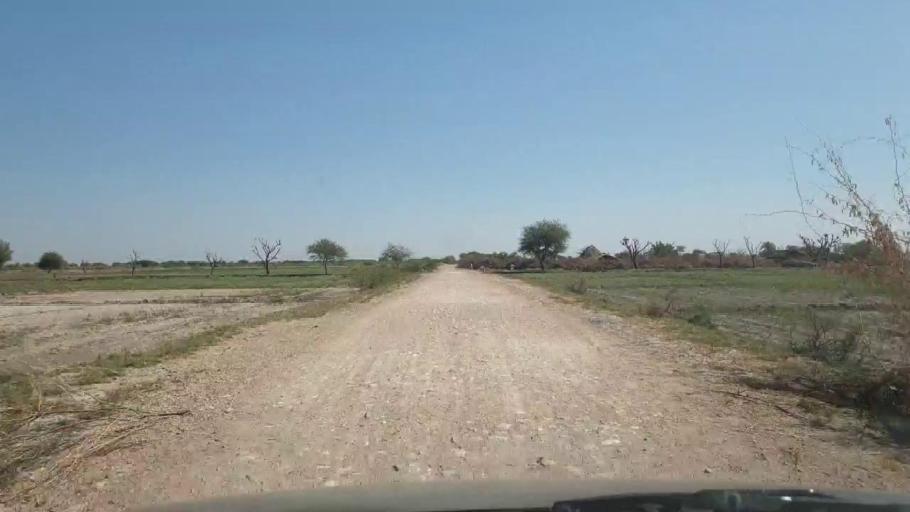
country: PK
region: Sindh
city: Dhoro Naro
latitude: 25.4587
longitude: 69.6092
